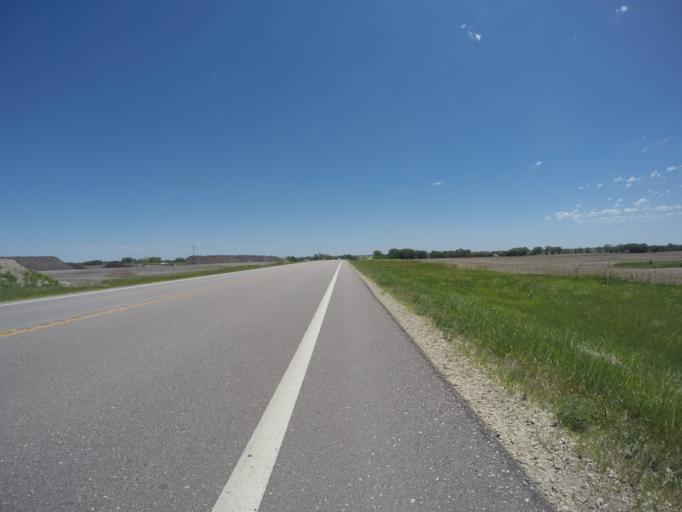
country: US
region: Kansas
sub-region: Republic County
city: Belleville
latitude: 39.8123
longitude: -97.6980
